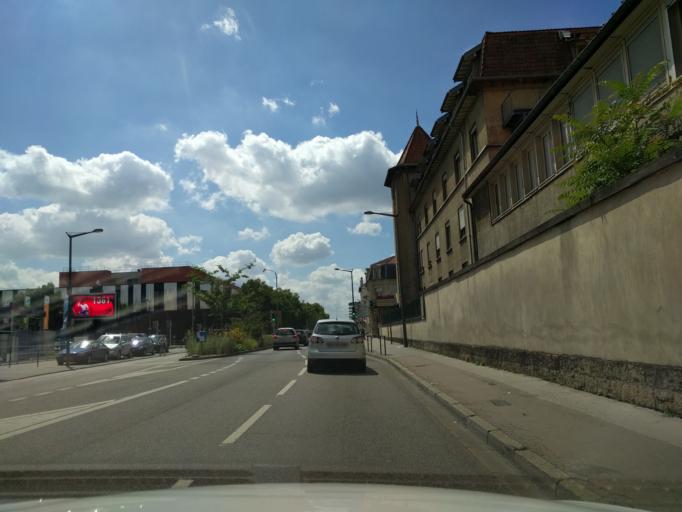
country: FR
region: Lorraine
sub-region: Departement de Meurthe-et-Moselle
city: Nancy
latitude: 48.6876
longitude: 6.1947
